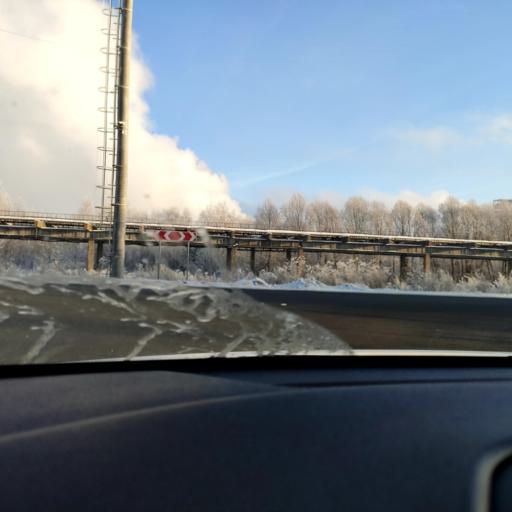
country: RU
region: Tatarstan
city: Osinovo
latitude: 55.8788
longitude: 48.9406
